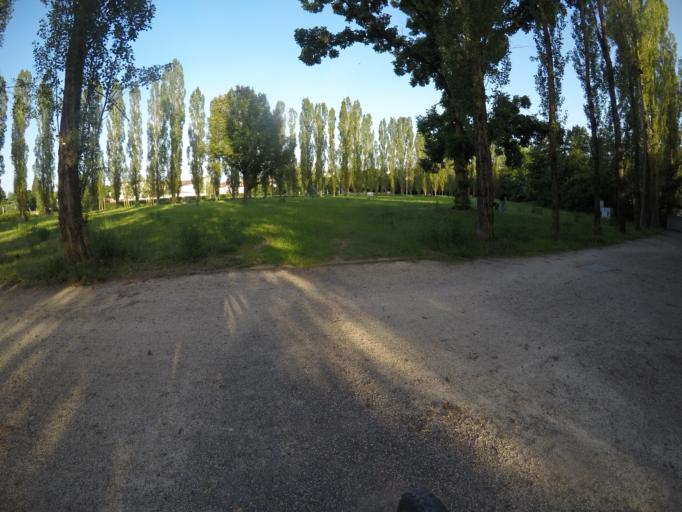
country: DE
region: Baden-Wuerttemberg
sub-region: Regierungsbezirk Stuttgart
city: Boeblingen
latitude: 48.6783
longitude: 9.0188
